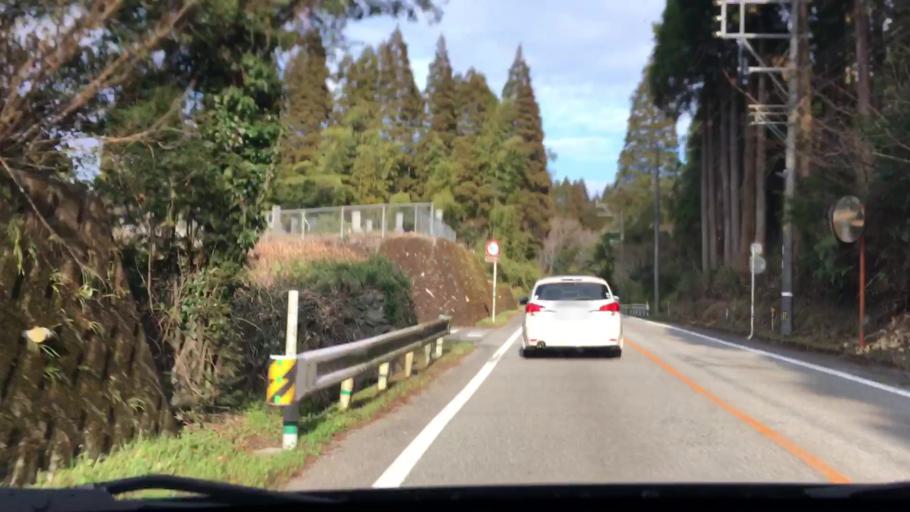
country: JP
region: Miyazaki
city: Nichinan
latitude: 31.7227
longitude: 131.3284
